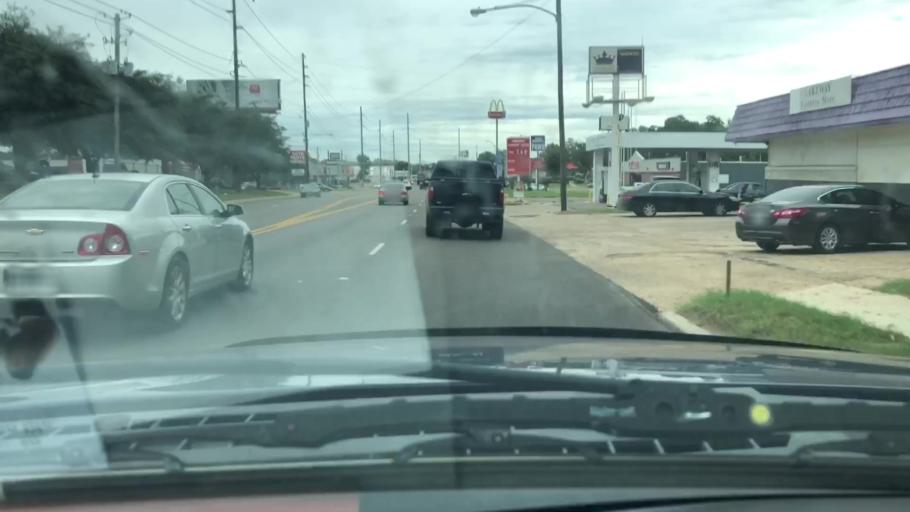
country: US
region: Texas
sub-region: Bowie County
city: Texarkana
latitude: 33.4349
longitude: -94.0651
